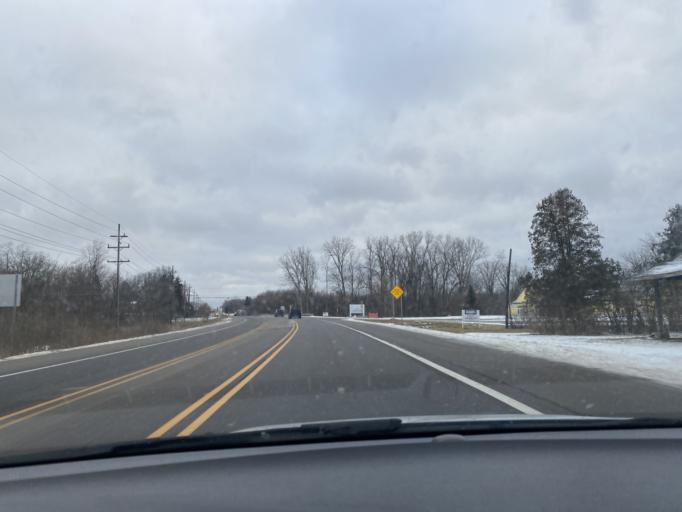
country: US
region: Michigan
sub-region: Lapeer County
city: Imlay City
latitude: 42.9897
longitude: -83.0694
